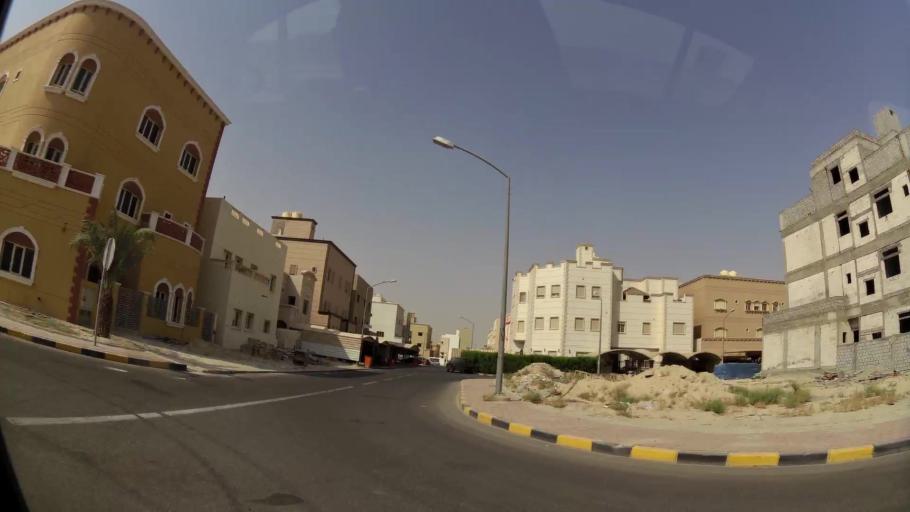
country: KW
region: Muhafazat al Jahra'
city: Al Jahra'
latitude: 29.3274
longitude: 47.7794
